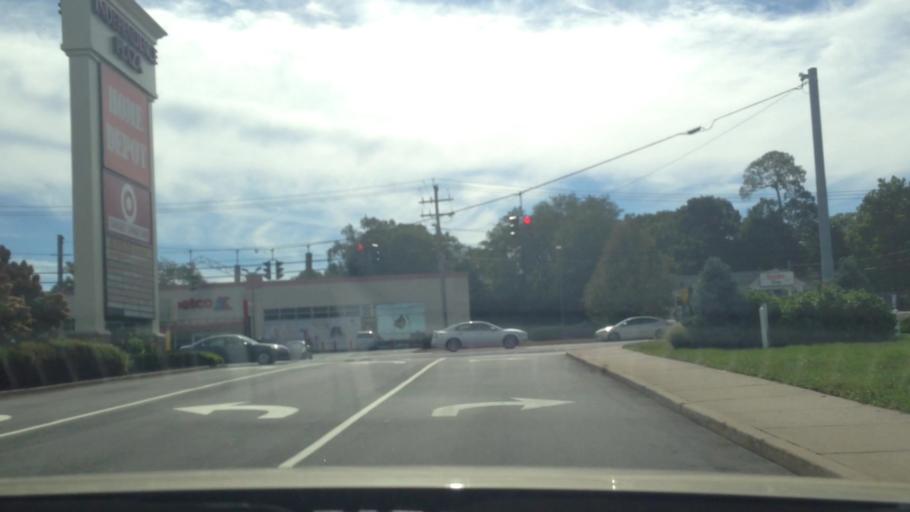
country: US
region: New York
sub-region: Suffolk County
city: Selden
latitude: 40.8637
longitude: -73.0521
